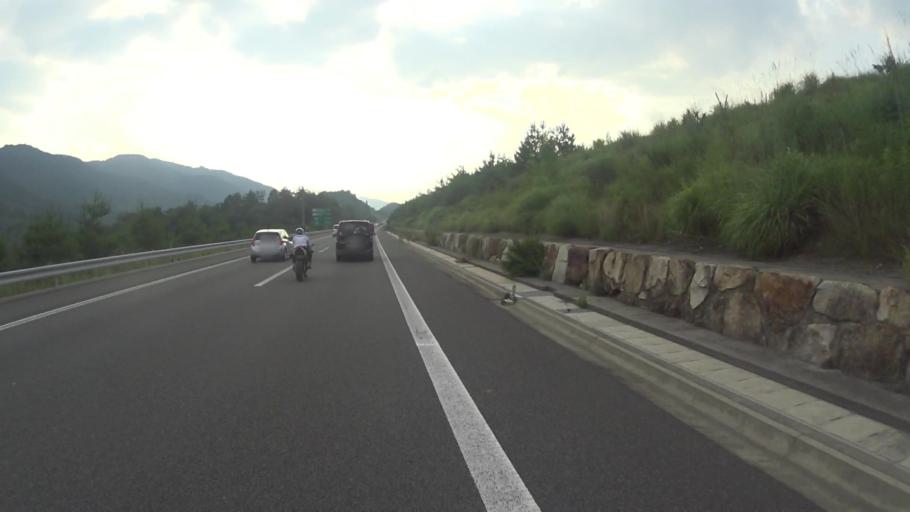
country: JP
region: Shiga Prefecture
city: Minakuchicho-matoba
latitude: 34.9281
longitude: 136.0675
